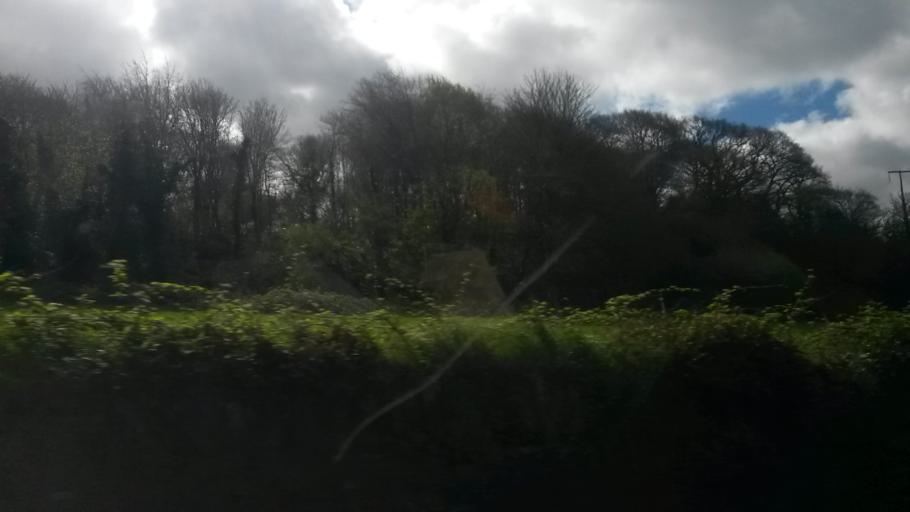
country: IE
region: Munster
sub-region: County Cork
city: Passage West
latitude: 51.8793
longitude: -8.3215
